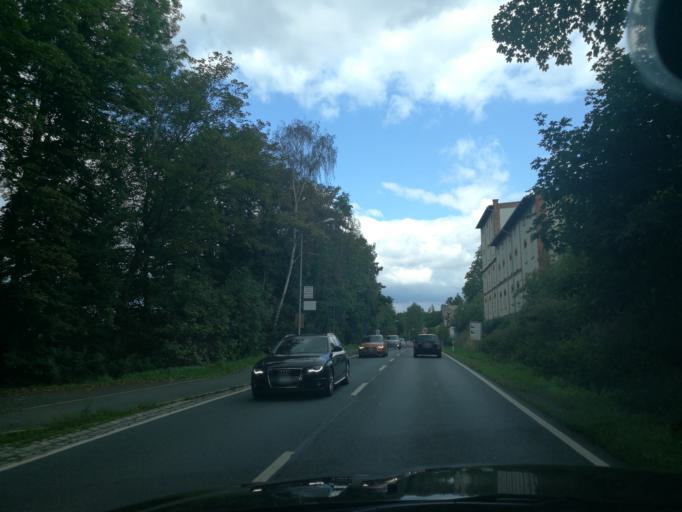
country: DE
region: Saxony
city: Oelsnitz
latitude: 50.4073
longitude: 12.1815
